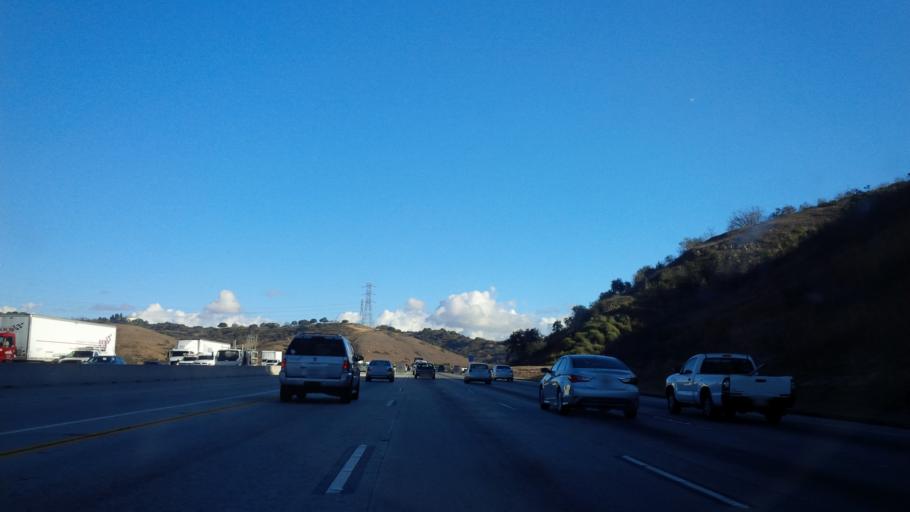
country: US
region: California
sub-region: Los Angeles County
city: Rowland Heights
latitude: 33.9512
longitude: -117.8643
